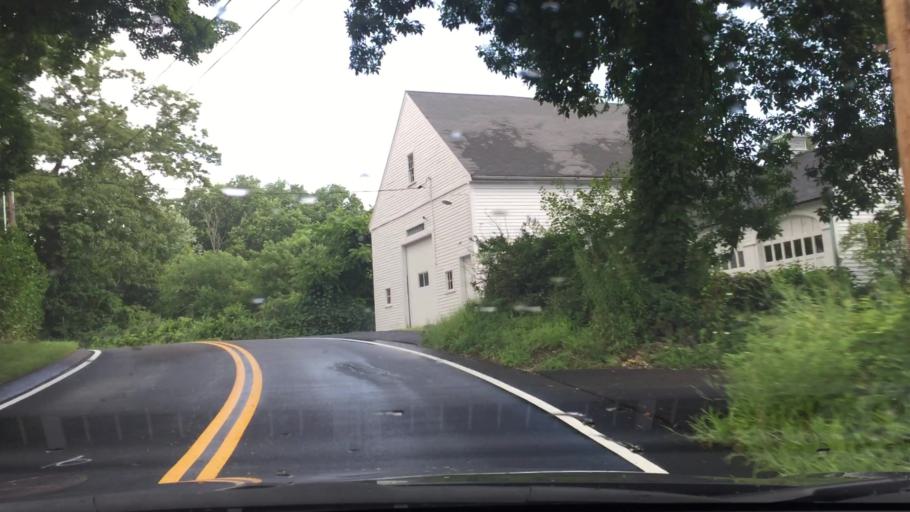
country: US
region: Massachusetts
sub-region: Middlesex County
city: Acton
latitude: 42.5131
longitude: -71.4505
